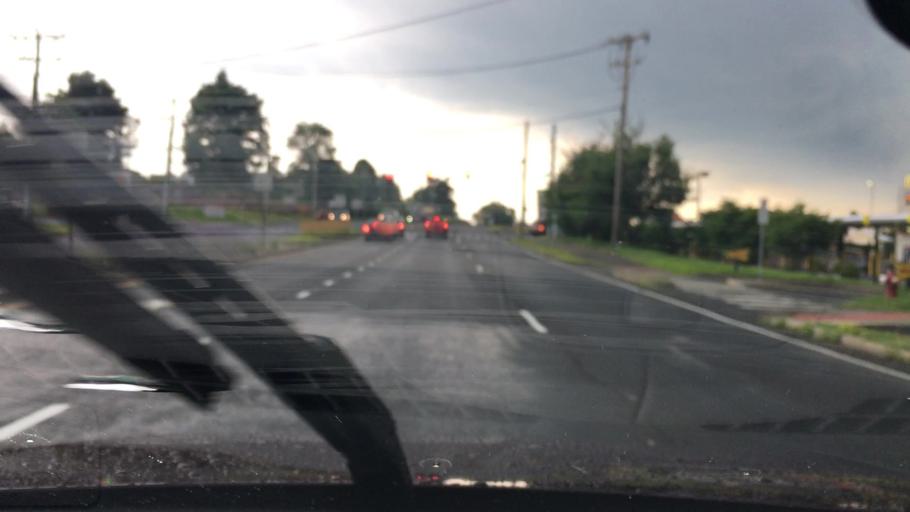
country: US
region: Connecticut
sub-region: Hartford County
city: Manchester
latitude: 41.7996
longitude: -72.5511
